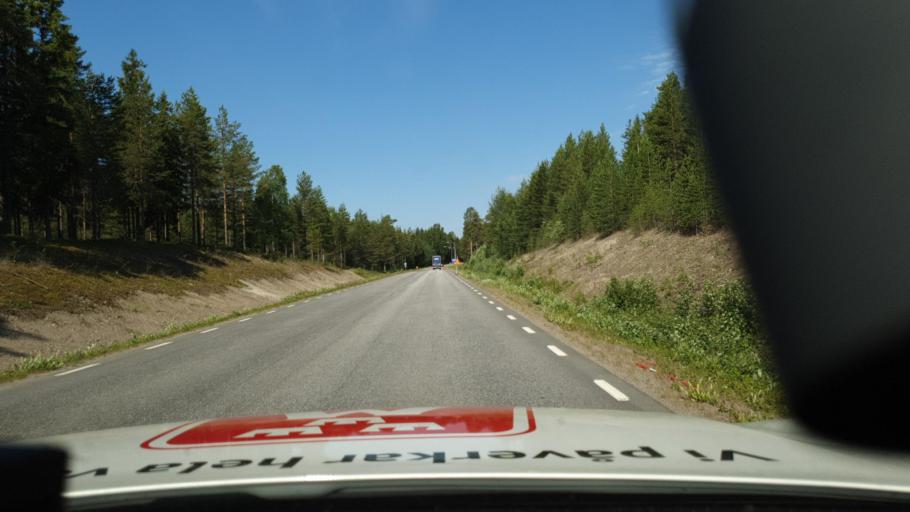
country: SE
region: Norrbotten
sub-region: Lulea Kommun
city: Ranea
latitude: 65.8612
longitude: 22.3172
